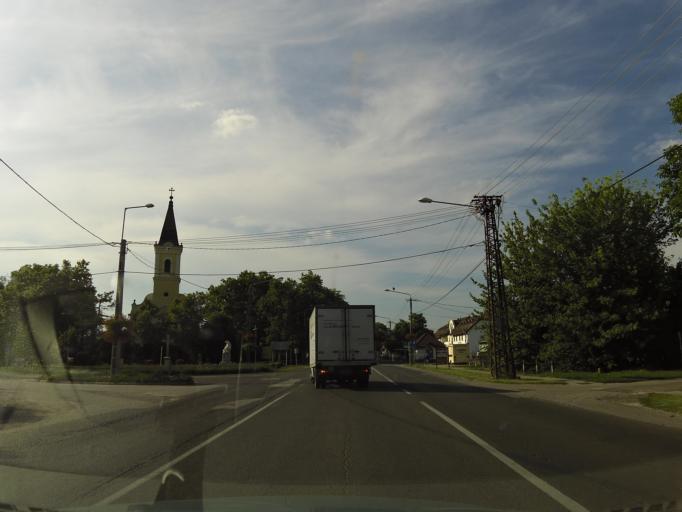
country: HU
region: Csongrad
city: Balastya
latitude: 46.4222
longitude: 20.0138
